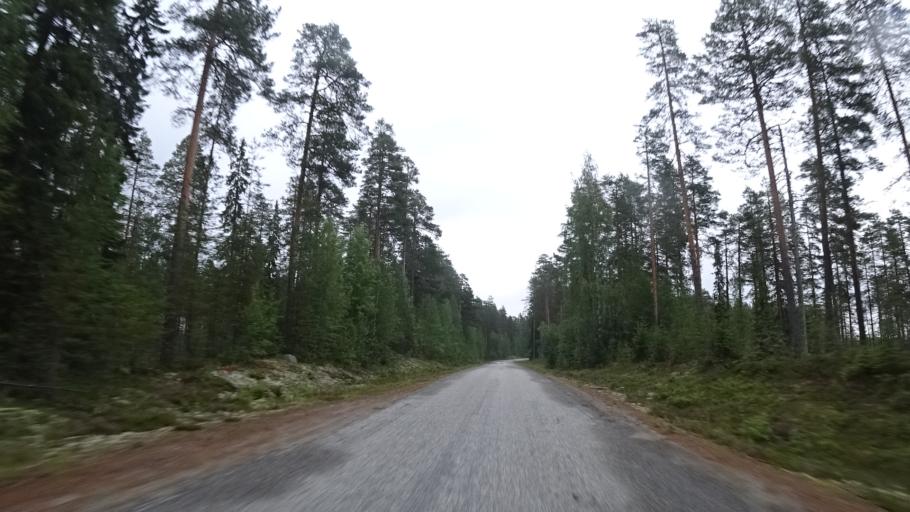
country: FI
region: North Karelia
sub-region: Joensuu
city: Ilomantsi
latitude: 63.2281
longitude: 30.8707
